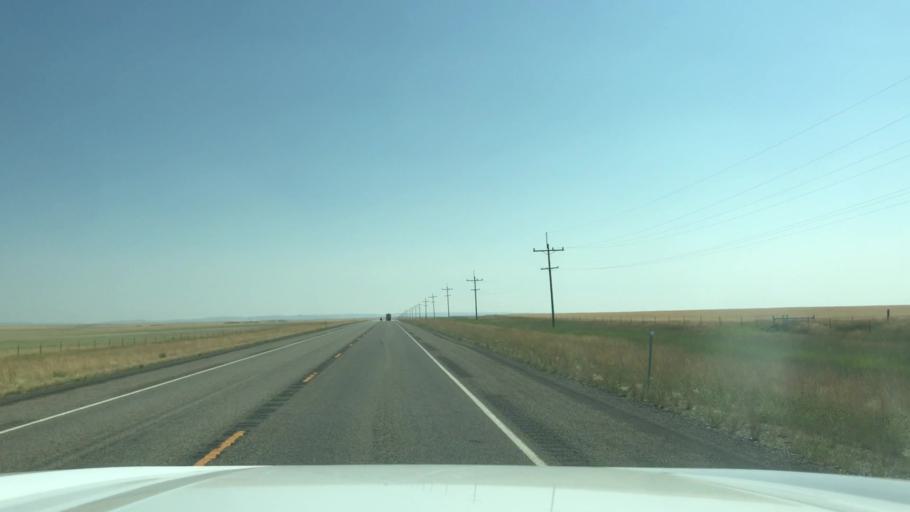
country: US
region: Montana
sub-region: Wheatland County
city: Harlowton
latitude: 46.5124
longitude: -109.7661
